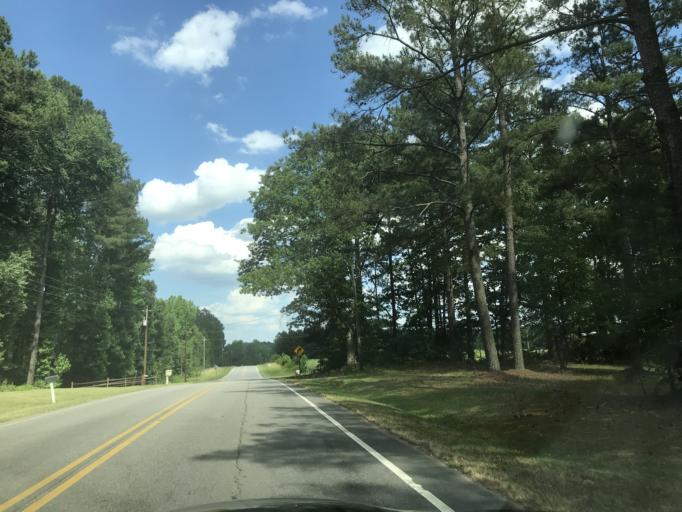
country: US
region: North Carolina
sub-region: Nash County
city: Spring Hope
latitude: 35.9211
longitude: -78.1781
